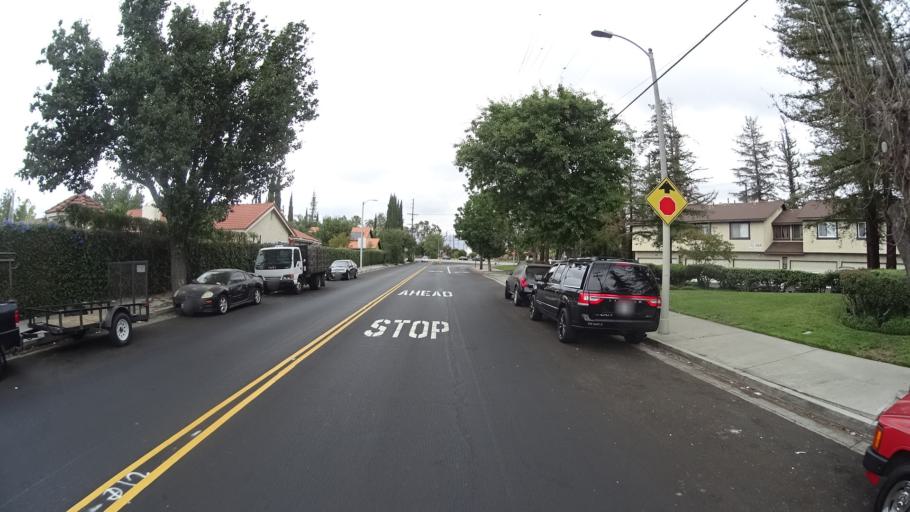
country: US
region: California
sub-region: Los Angeles County
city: San Fernando
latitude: 34.2486
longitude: -118.4503
